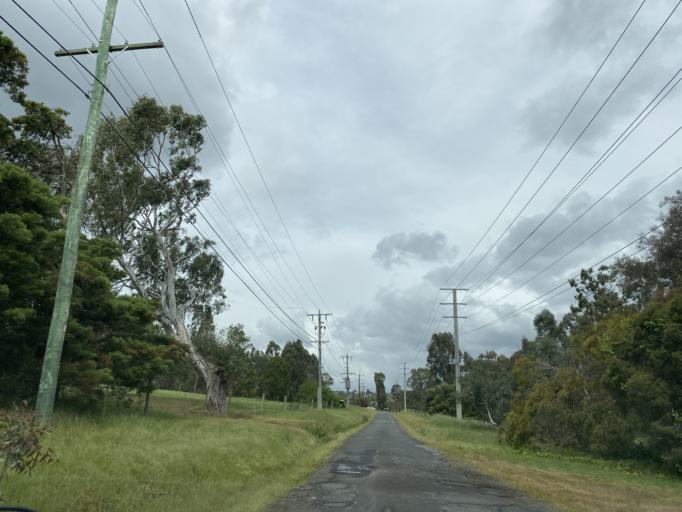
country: AU
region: Victoria
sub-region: Banyule
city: Darch
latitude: -37.7515
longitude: 145.1130
